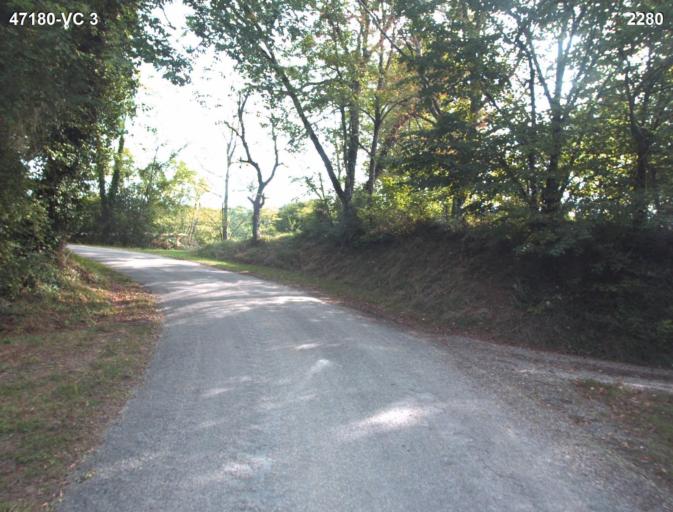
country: FR
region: Aquitaine
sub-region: Departement du Lot-et-Garonne
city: Sainte-Colombe-en-Bruilhois
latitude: 44.1507
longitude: 0.4415
